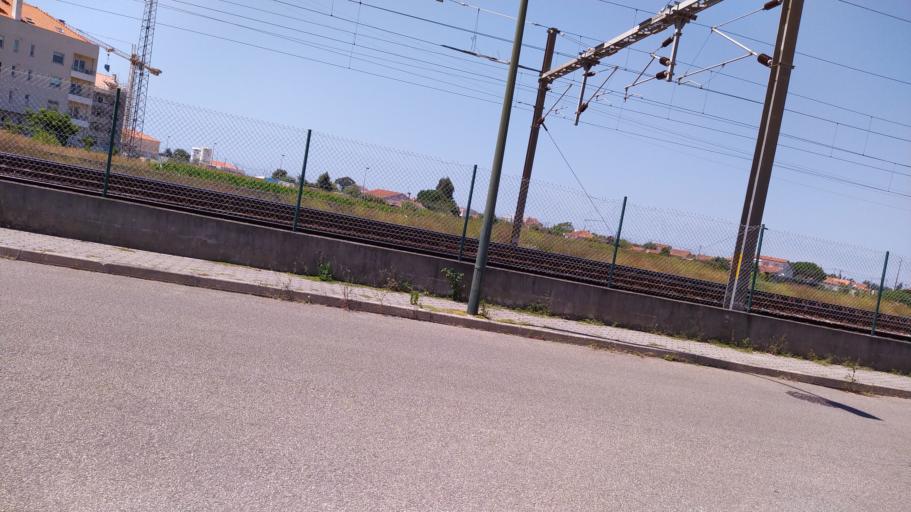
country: PT
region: Aveiro
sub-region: Aveiro
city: Aveiro
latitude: 40.6482
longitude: -8.6369
